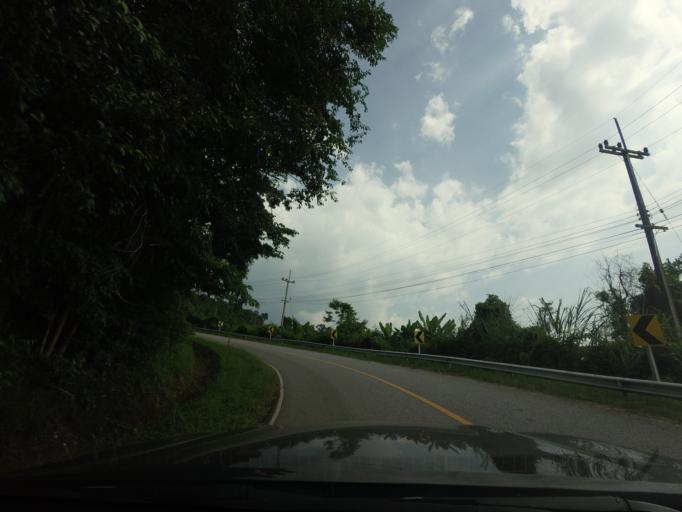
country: TH
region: Phitsanulok
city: Nakhon Thai
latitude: 17.0214
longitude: 100.9425
